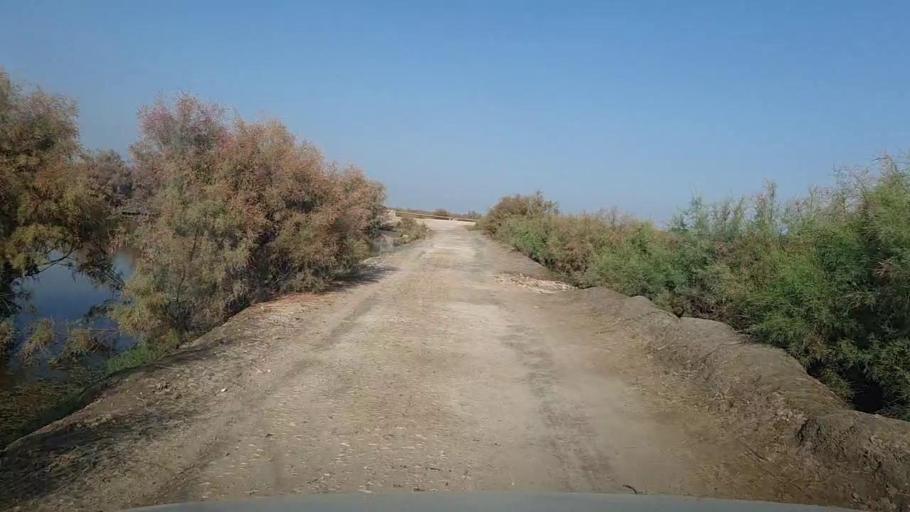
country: PK
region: Sindh
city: Kandhkot
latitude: 28.2816
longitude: 69.3293
